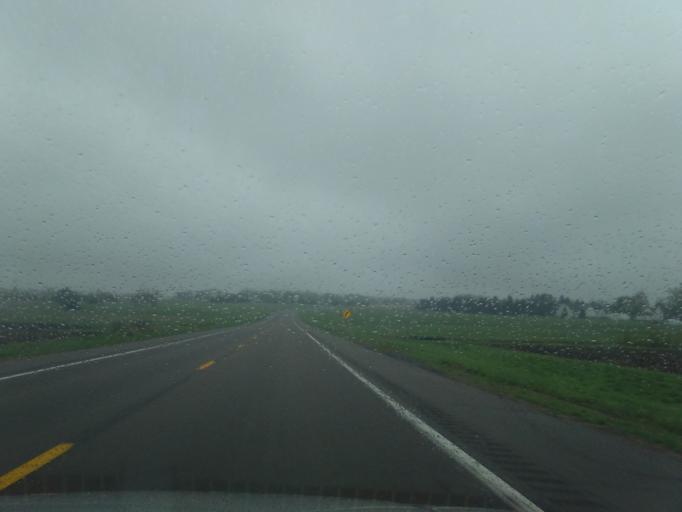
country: US
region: Nebraska
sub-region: Madison County
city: Norfolk
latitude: 42.0827
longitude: -97.3250
